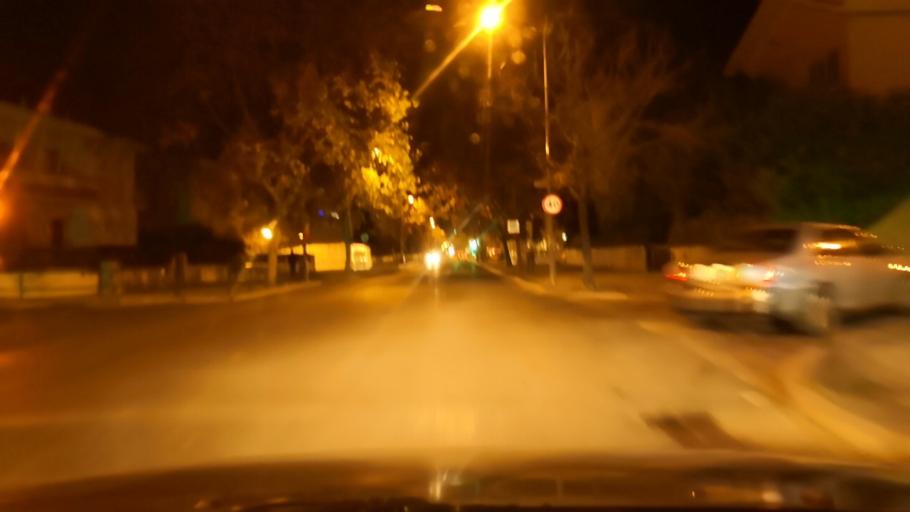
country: PT
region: Setubal
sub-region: Setubal
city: Setubal
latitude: 38.5349
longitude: -8.8934
